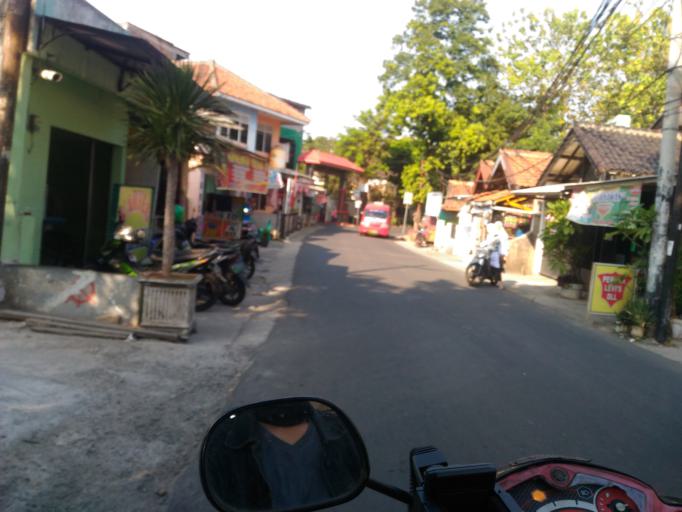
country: ID
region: West Java
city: Depok
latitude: -6.3267
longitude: 106.8531
